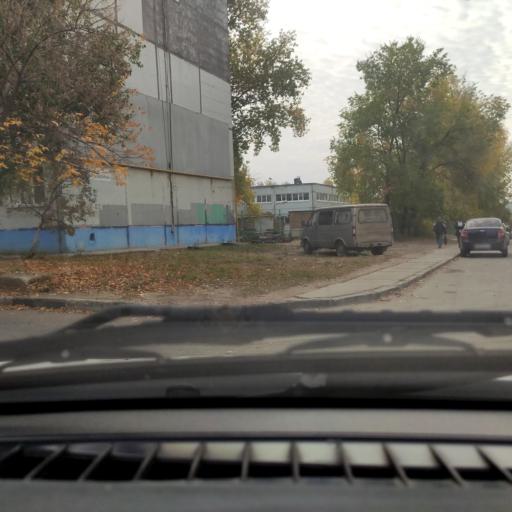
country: RU
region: Samara
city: Zhigulevsk
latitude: 53.4805
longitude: 49.4814
